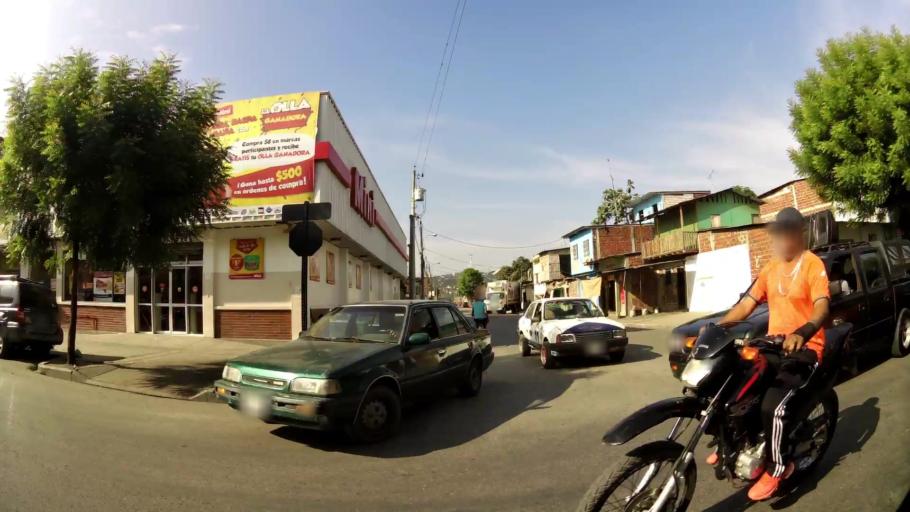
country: EC
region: Guayas
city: Eloy Alfaro
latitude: -2.0682
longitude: -79.9325
